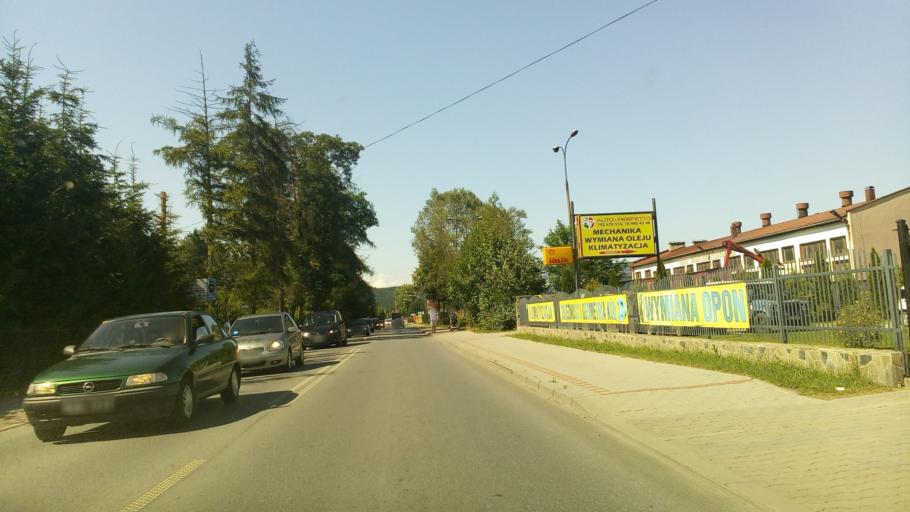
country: PL
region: Lesser Poland Voivodeship
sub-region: Powiat nowosadecki
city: Chelmiec
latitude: 49.6265
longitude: 20.6679
